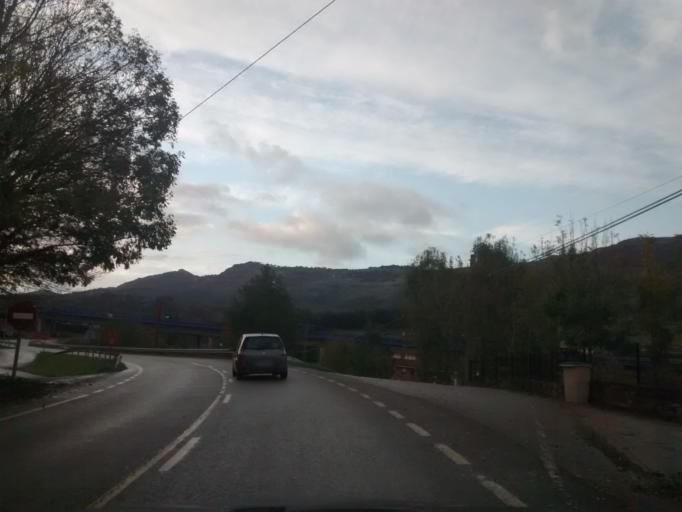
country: ES
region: Cantabria
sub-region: Provincia de Cantabria
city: Lierganes
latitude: 43.3554
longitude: -3.7653
